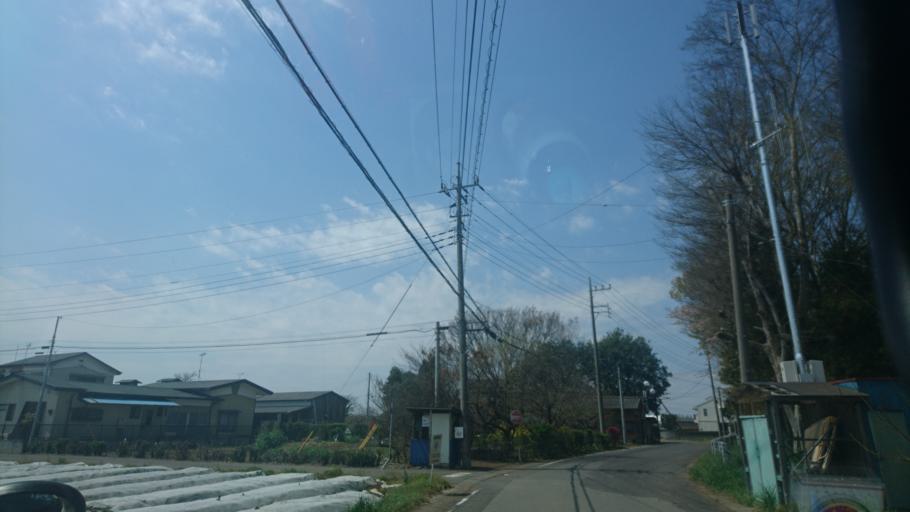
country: JP
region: Ibaraki
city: Yuki
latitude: 36.2202
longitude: 139.9211
